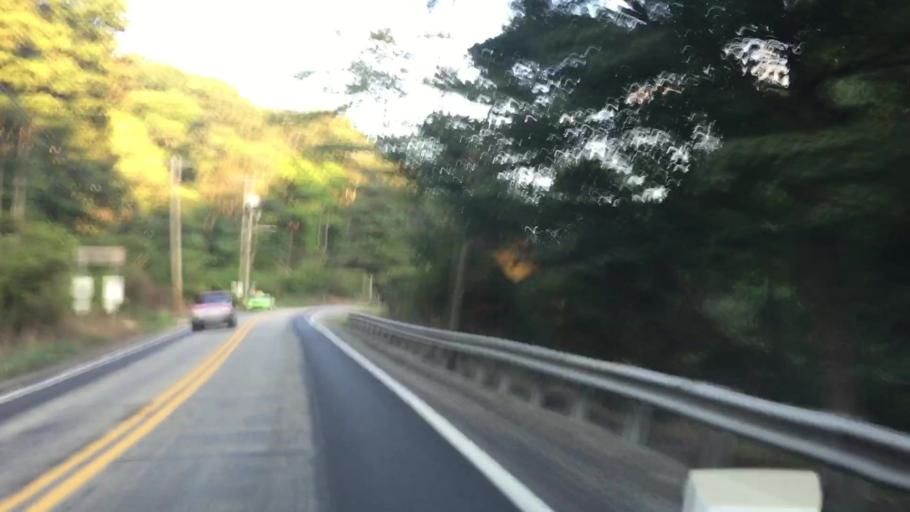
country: US
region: Pennsylvania
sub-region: Allegheny County
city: West View
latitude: 40.5334
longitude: -80.0483
